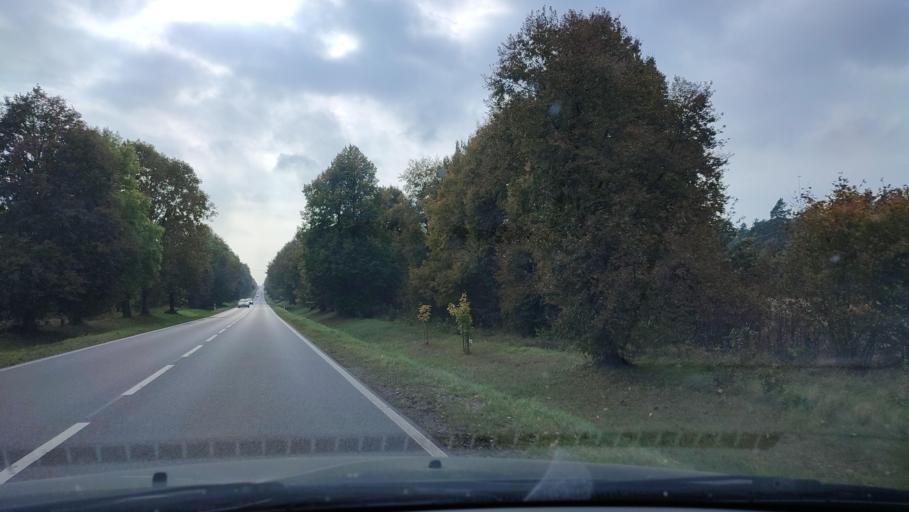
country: PL
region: Warmian-Masurian Voivodeship
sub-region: Powiat nidzicki
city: Kozlowo
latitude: 53.3450
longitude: 20.3478
